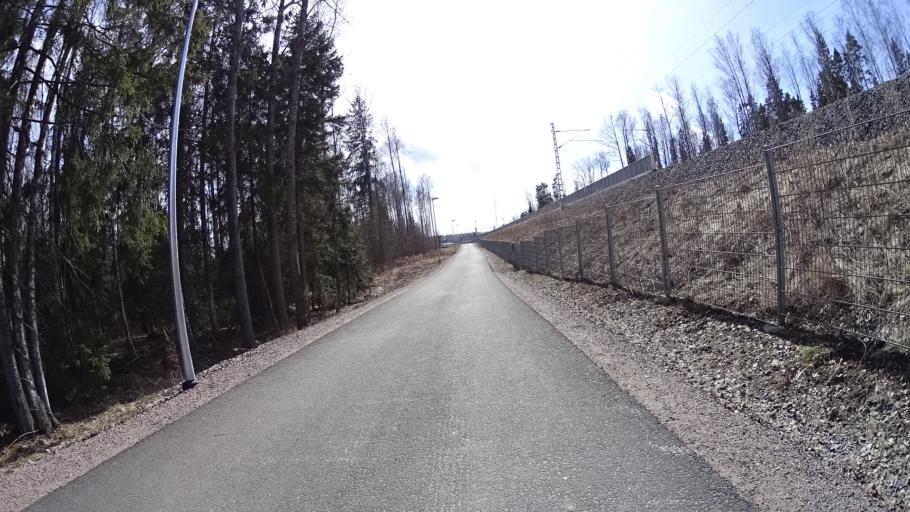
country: FI
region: Uusimaa
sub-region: Helsinki
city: Kilo
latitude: 60.3008
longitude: 24.8426
